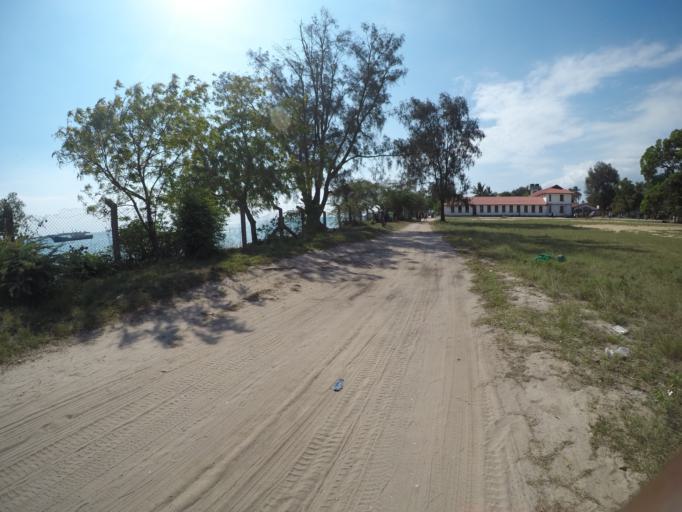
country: TZ
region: Zanzibar Urban/West
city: Zanzibar
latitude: -6.1213
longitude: 39.2126
